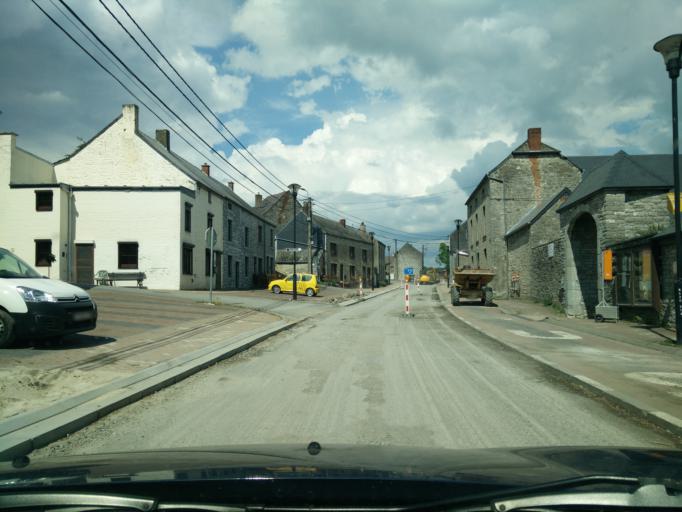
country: BE
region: Wallonia
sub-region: Province de Namur
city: Couvin
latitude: 50.0776
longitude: 4.5483
